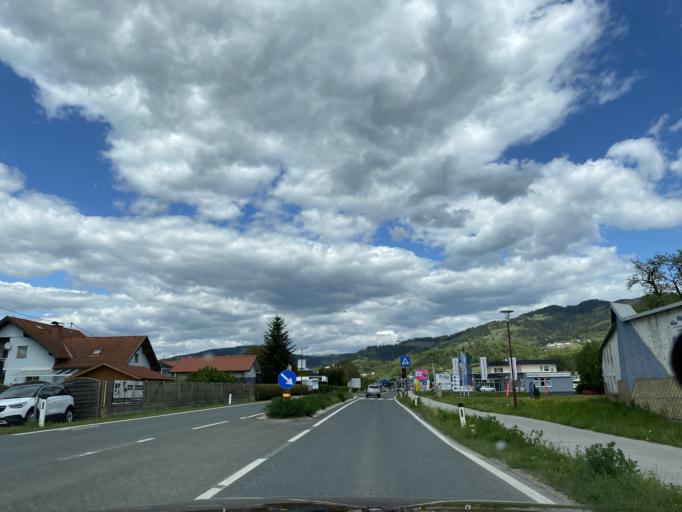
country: AT
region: Carinthia
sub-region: Politischer Bezirk Wolfsberg
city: Wolfsberg
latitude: 46.8201
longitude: 14.8367
